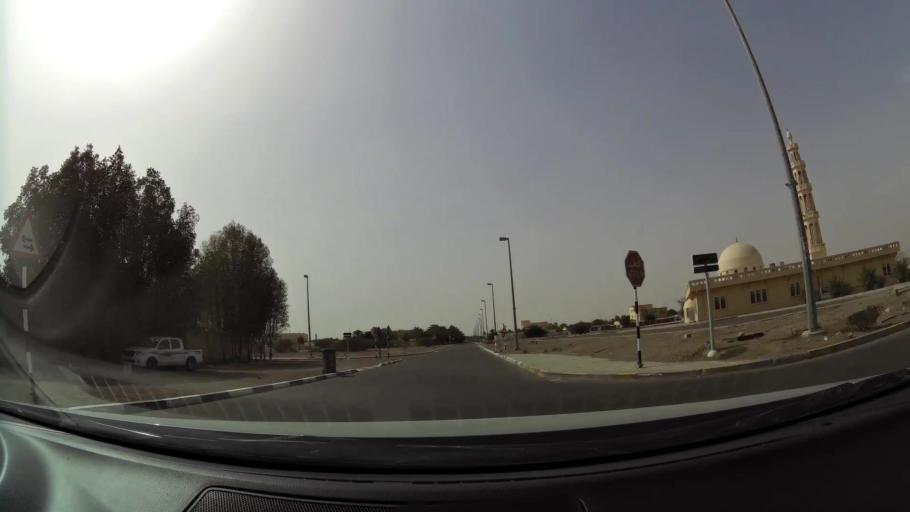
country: AE
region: Abu Dhabi
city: Al Ain
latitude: 24.1845
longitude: 55.6201
